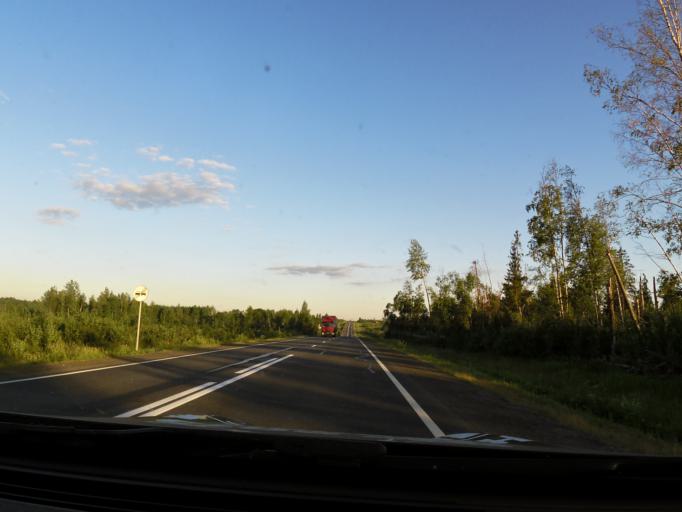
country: RU
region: Jaroslavl
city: Prechistoye
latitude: 58.5995
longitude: 40.3419
